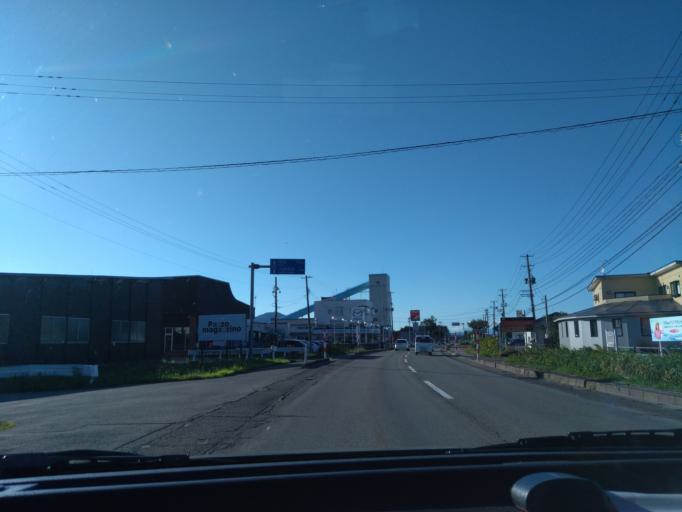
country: JP
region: Akita
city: Omagari
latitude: 39.4291
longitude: 140.4872
